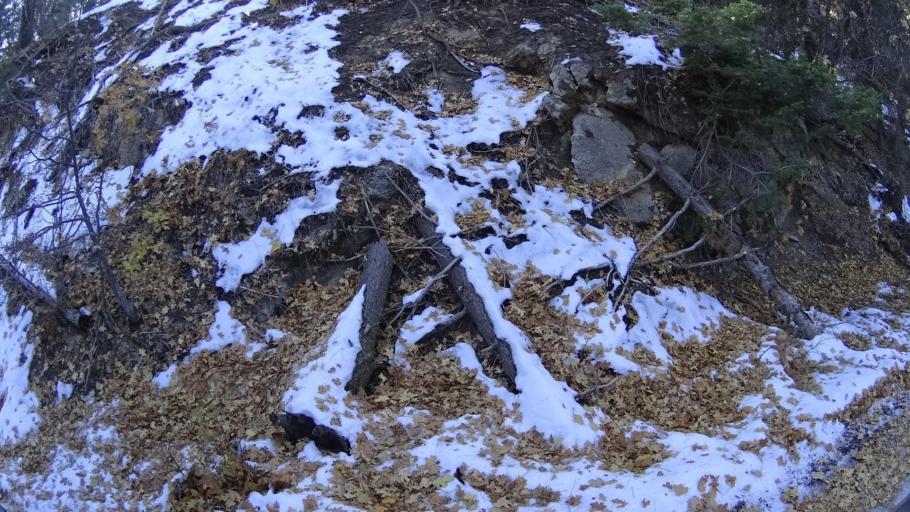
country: US
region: California
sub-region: Kern County
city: Bodfish
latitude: 35.4769
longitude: -118.6398
